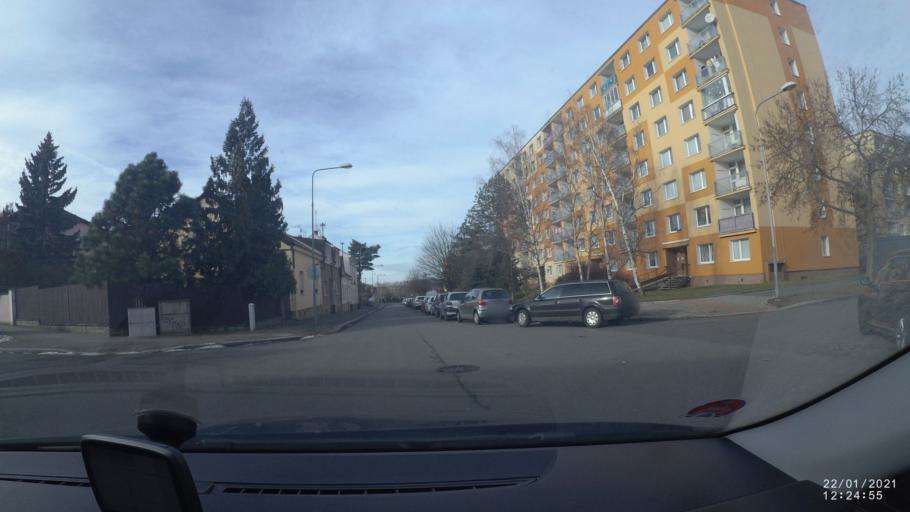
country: CZ
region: Plzensky
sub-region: Okres Plzen-Mesto
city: Pilsen
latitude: 49.7566
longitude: 13.4226
